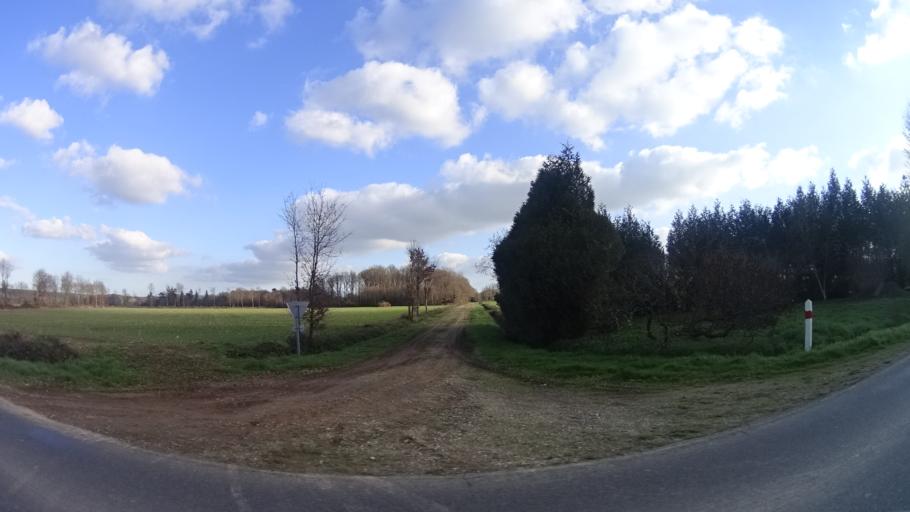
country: FR
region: Pays de la Loire
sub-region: Departement de la Loire-Atlantique
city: Guemene-Penfao
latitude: 47.6133
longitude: -1.8392
